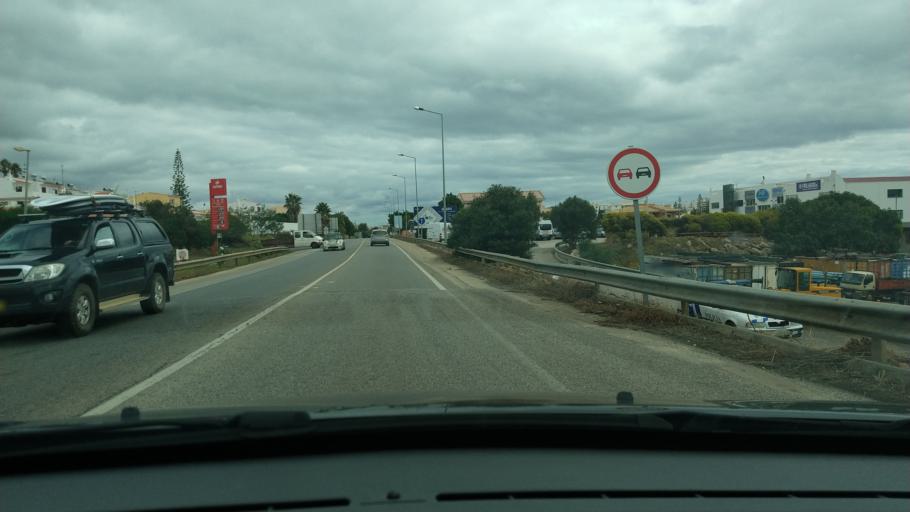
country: PT
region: Faro
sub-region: Lagos
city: Lagos
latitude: 37.1016
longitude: -8.6930
